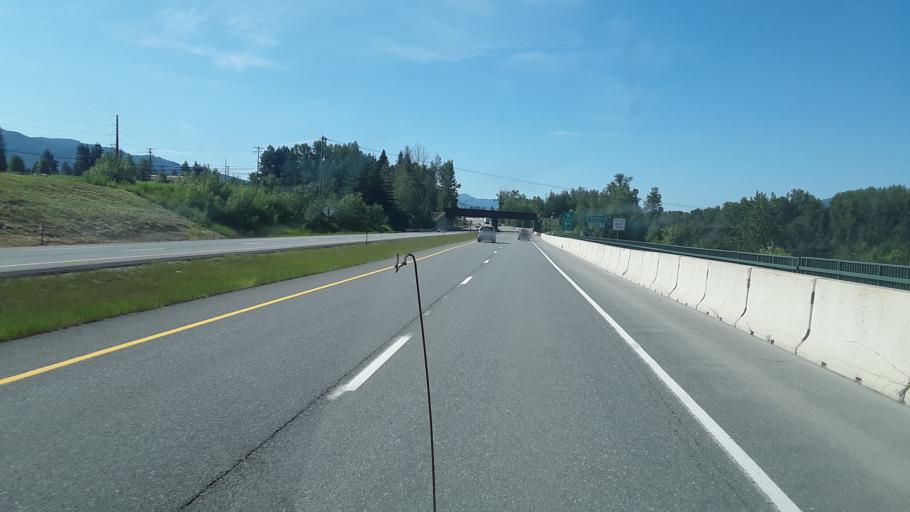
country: US
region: Idaho
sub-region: Bonner County
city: Ponderay
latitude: 48.2967
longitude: -116.5486
